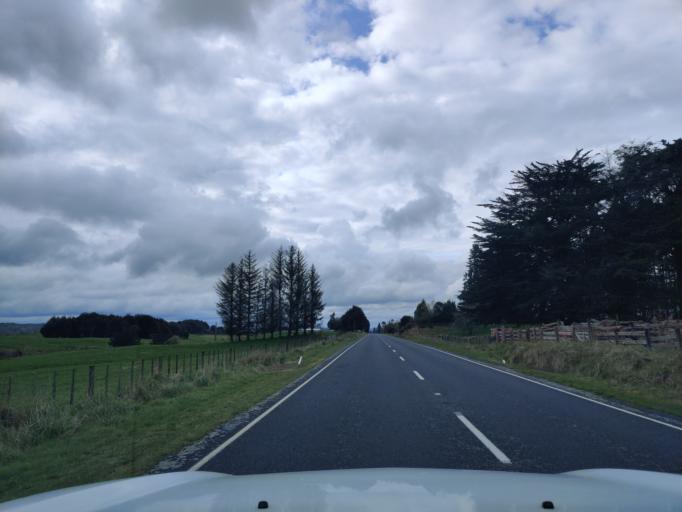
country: NZ
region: Waikato
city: Turangi
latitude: -39.0447
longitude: 175.3834
